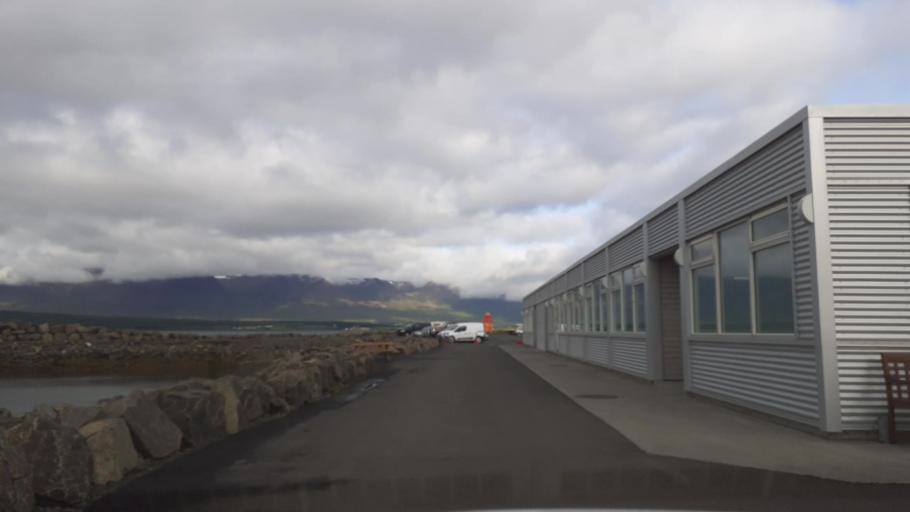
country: IS
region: Northeast
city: Akureyri
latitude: 65.7426
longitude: -18.0868
